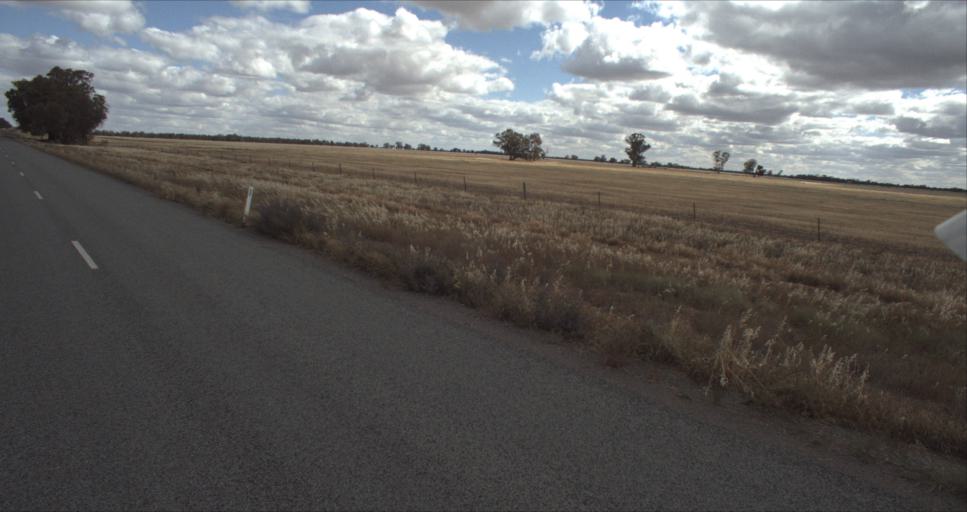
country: AU
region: New South Wales
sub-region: Leeton
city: Leeton
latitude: -34.6698
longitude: 146.3477
